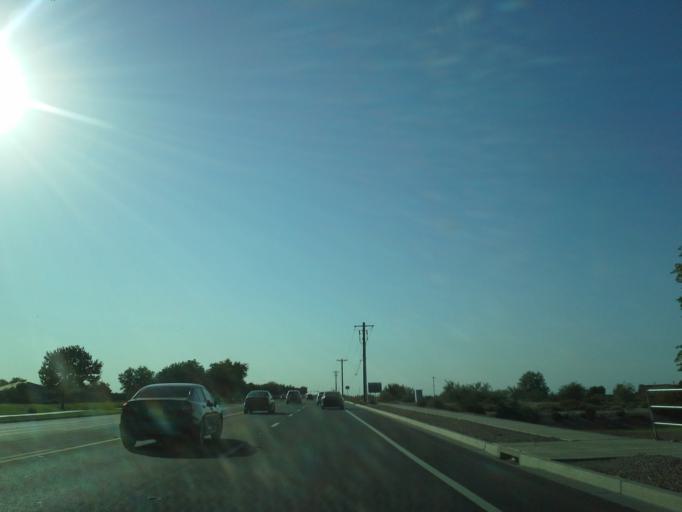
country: US
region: Arizona
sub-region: Pinal County
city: San Tan Valley
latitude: 33.1857
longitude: -111.5930
